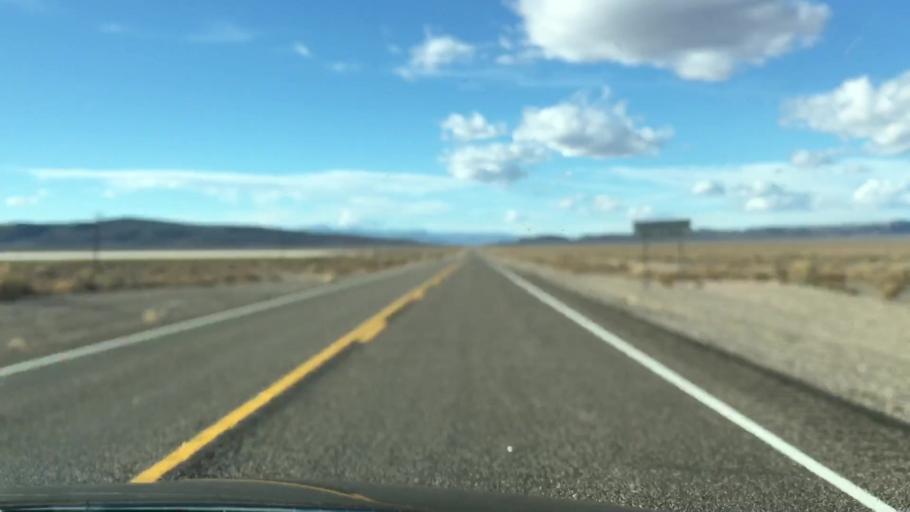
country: US
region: Nevada
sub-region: Nye County
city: Beatty
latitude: 37.1392
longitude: -116.8570
